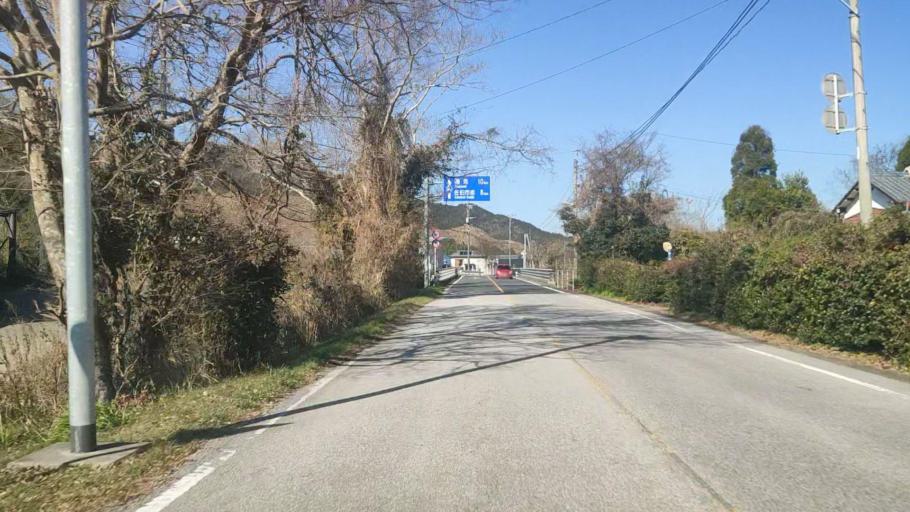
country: JP
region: Oita
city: Saiki
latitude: 32.9070
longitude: 131.9313
